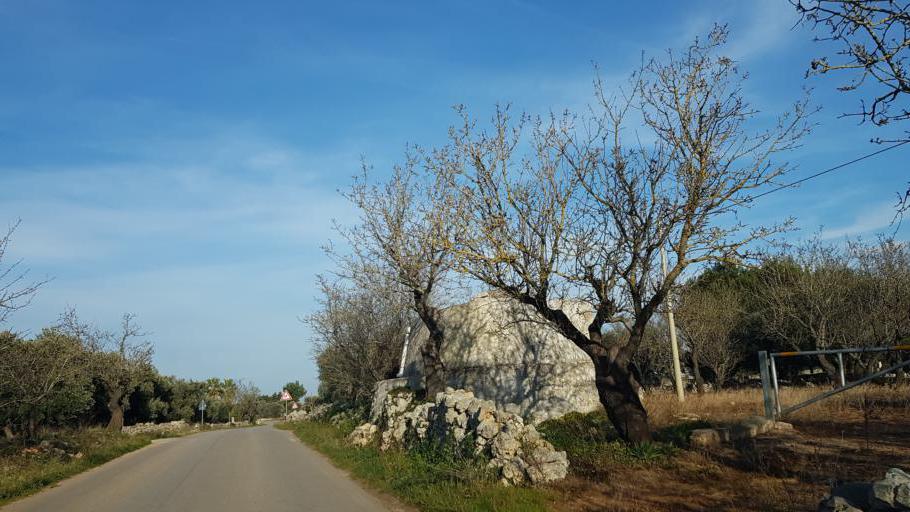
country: IT
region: Apulia
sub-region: Provincia di Brindisi
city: Carovigno
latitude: 40.7019
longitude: 17.6788
